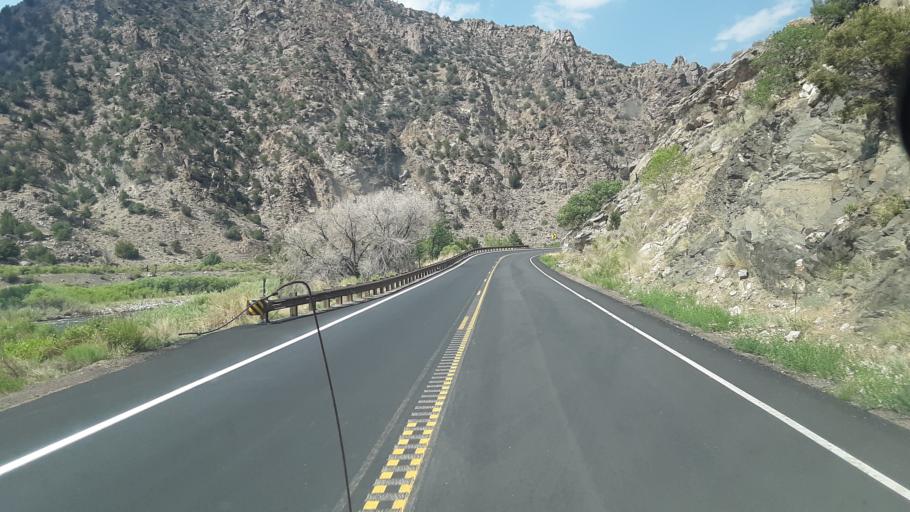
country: US
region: Colorado
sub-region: Fremont County
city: Canon City
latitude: 38.4435
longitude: -105.5291
